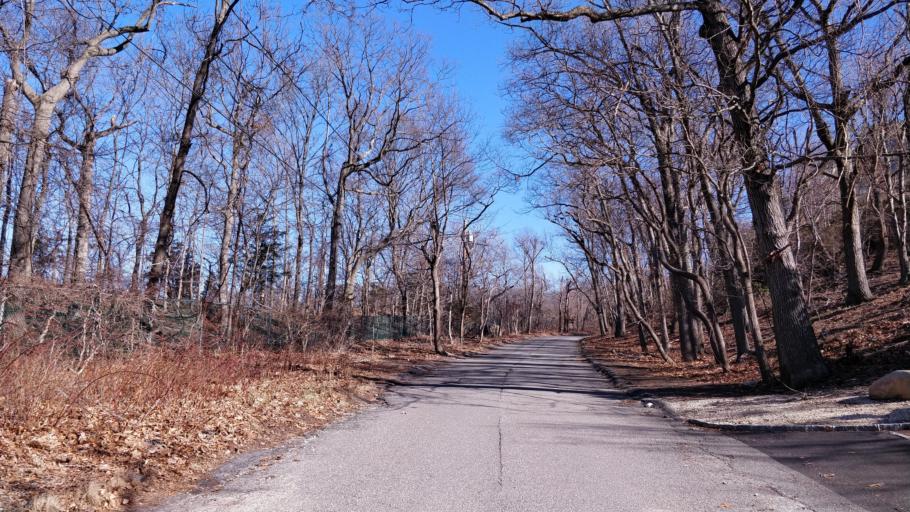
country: US
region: New York
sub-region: Suffolk County
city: Port Jefferson
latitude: 40.9672
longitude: -73.0766
